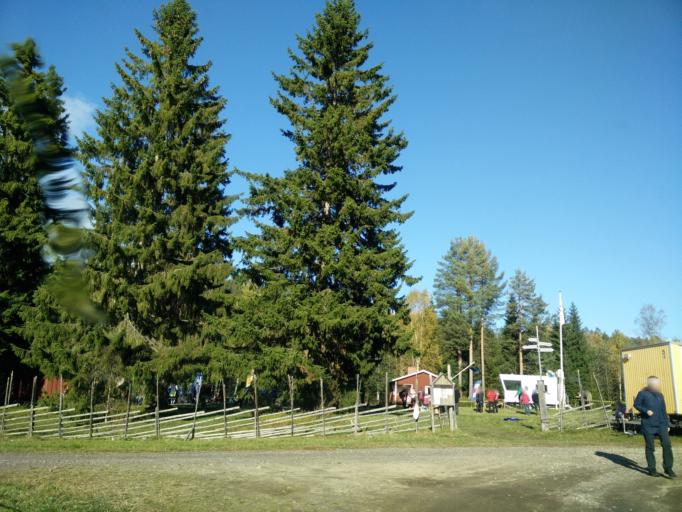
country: SE
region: Vaesternorrland
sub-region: Sundsvalls Kommun
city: Matfors
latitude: 62.3348
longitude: 16.8573
